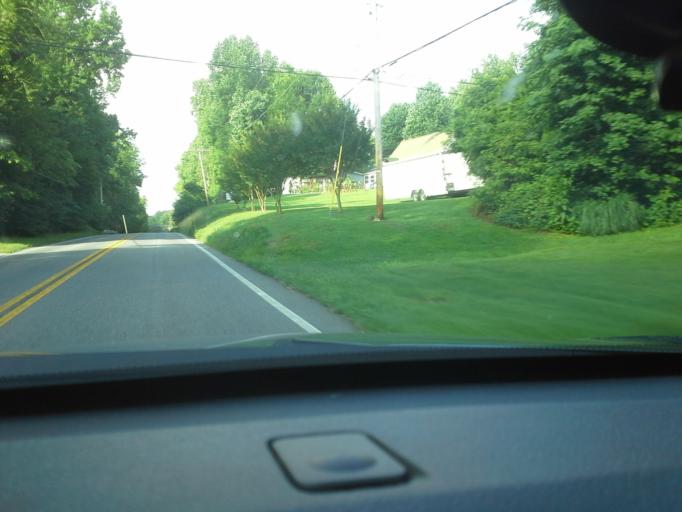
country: US
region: Maryland
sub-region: Calvert County
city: Chesapeake Beach
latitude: 38.6338
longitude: -76.5299
